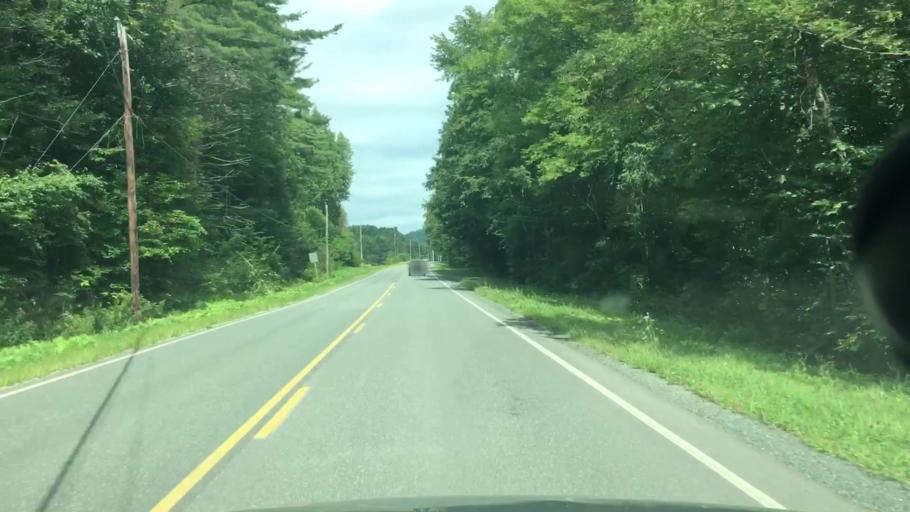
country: US
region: Massachusetts
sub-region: Franklin County
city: Colrain
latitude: 42.7189
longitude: -72.7078
